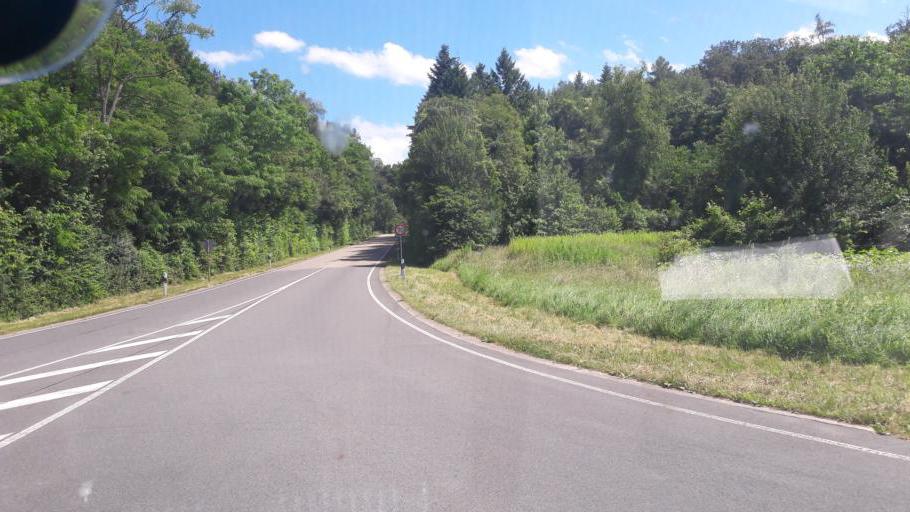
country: DE
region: Baden-Wuerttemberg
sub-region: Karlsruhe Region
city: Bruchsal
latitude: 49.1049
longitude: 8.5703
